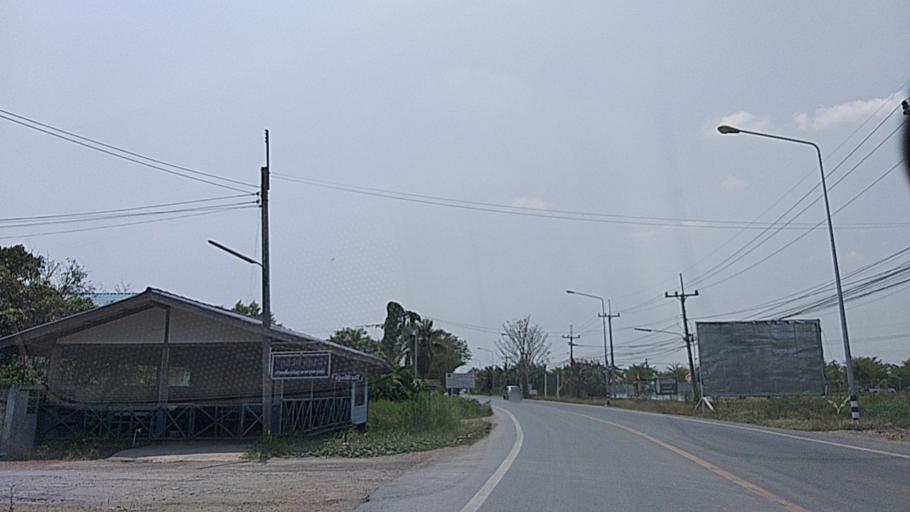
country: TH
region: Chachoengsao
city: Bang Nam Priao
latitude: 13.9404
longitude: 100.9786
